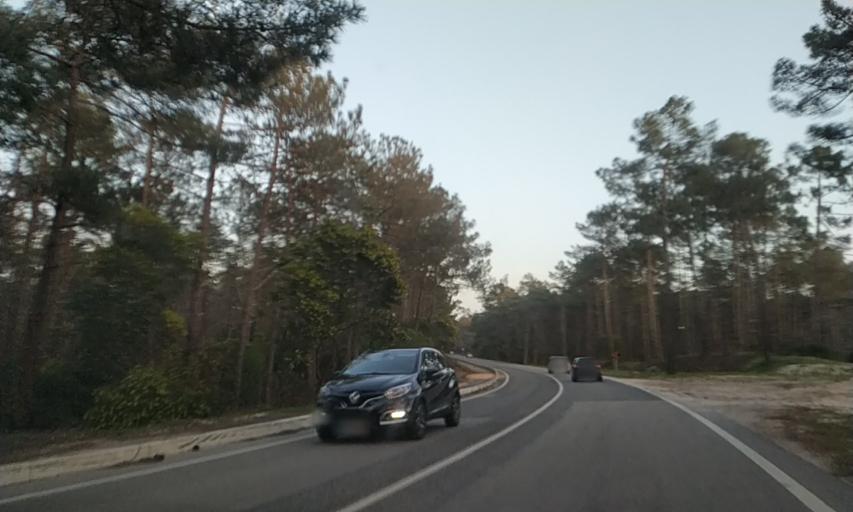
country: PT
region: Leiria
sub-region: Alcobaca
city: Pataias
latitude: 39.7531
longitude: -9.0227
